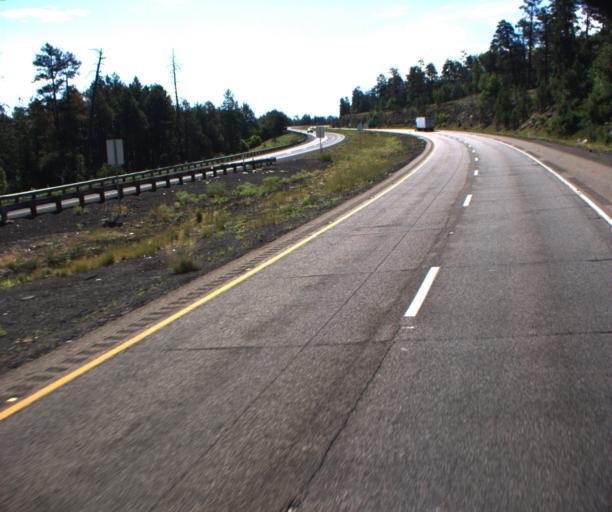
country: US
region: Arizona
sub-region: Coconino County
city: Sedona
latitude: 34.8649
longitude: -111.6262
